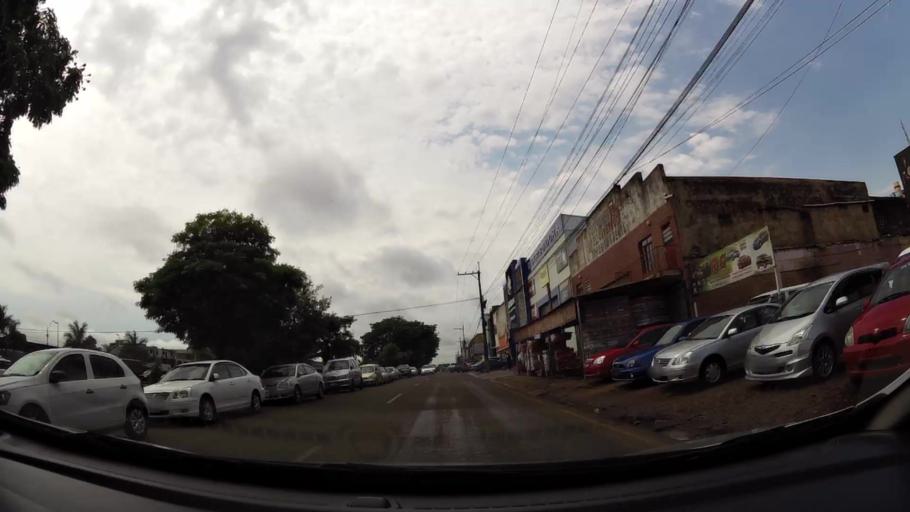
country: PY
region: Alto Parana
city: Ciudad del Este
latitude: -25.4983
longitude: -54.6658
